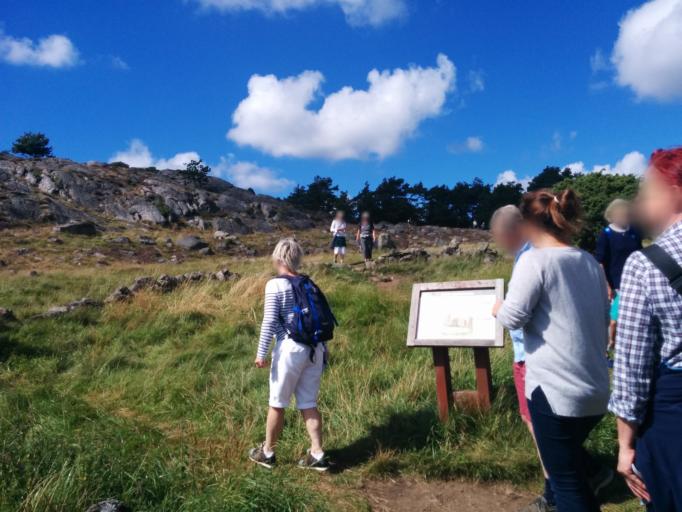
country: SE
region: Vaestra Goetaland
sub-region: Tjorns Kommun
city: Skaerhamn
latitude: 58.0303
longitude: 11.5540
